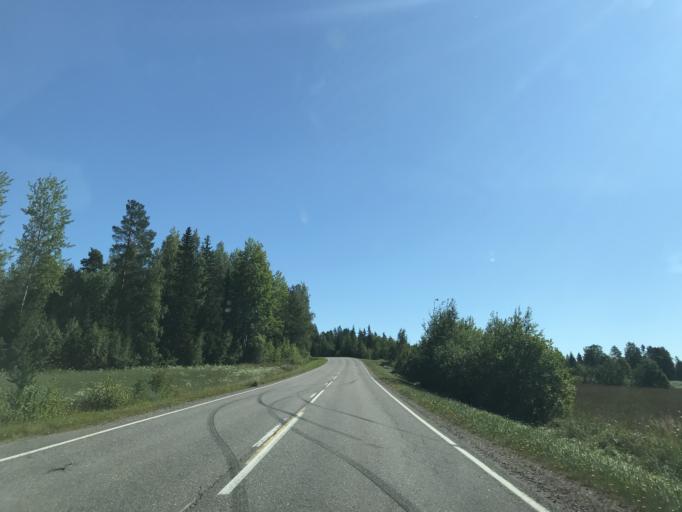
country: FI
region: Paijanne Tavastia
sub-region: Lahti
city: Orimattila
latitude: 60.8098
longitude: 25.7115
